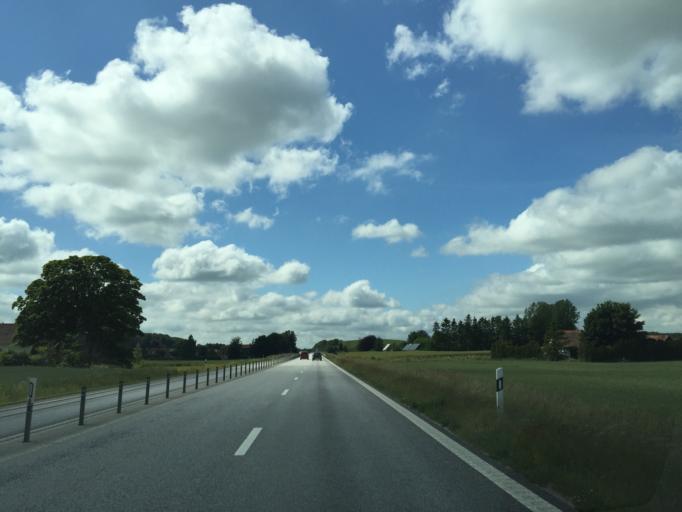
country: SE
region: Skane
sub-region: Skurups Kommun
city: Skurup
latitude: 55.4935
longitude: 13.5175
